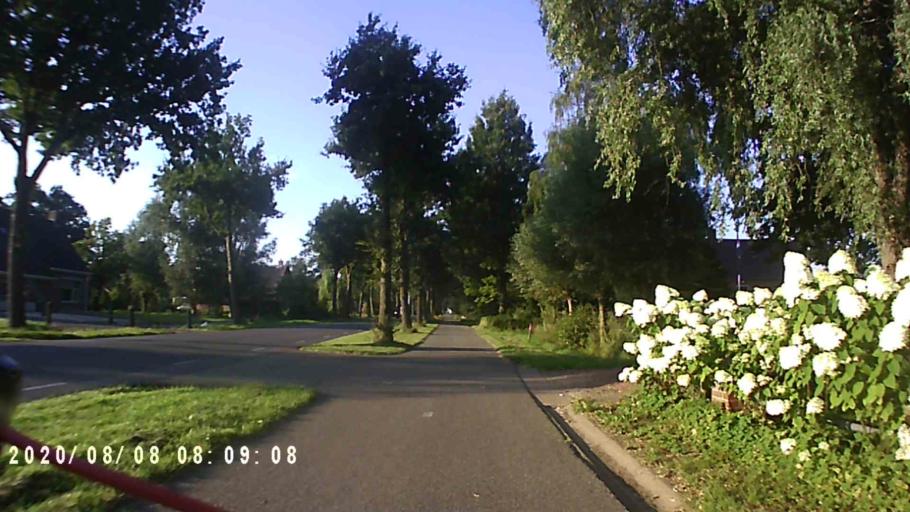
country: NL
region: Groningen
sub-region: Gemeente Leek
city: Leek
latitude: 53.1112
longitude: 6.3455
